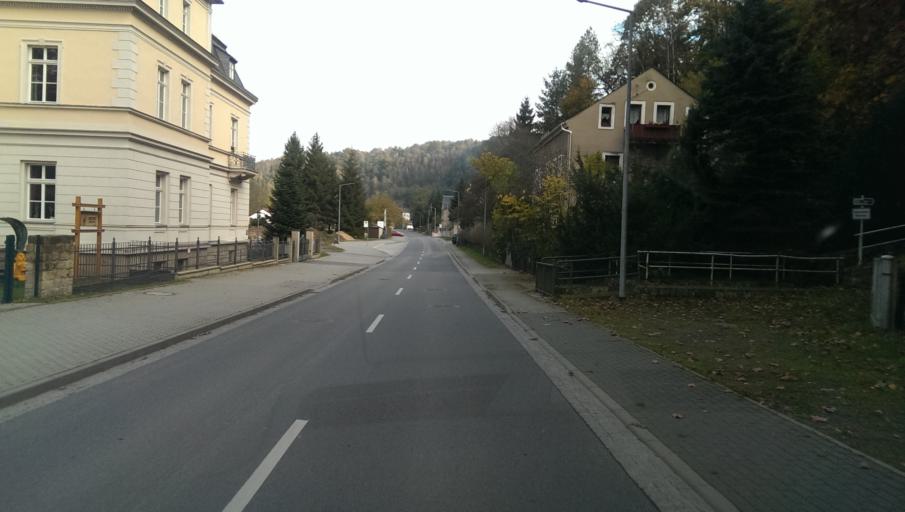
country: DE
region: Saxony
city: Rathmannsdorf
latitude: 50.9290
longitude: 14.1315
